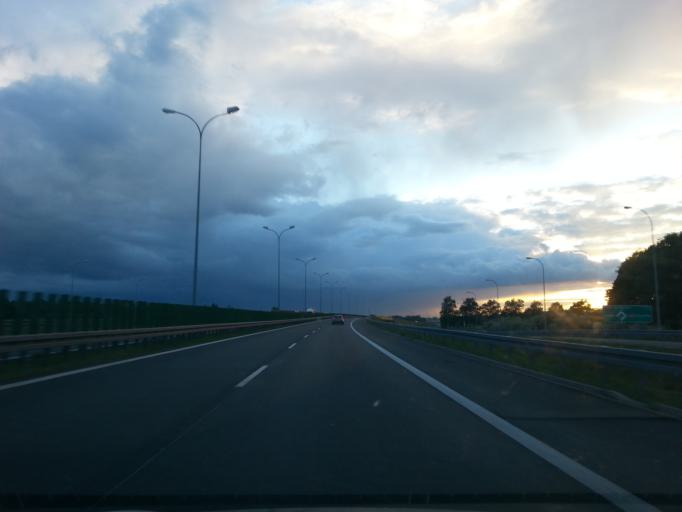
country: PL
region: Lower Silesian Voivodeship
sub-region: Powiat olesnicki
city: Olesnica
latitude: 51.2264
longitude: 17.4441
